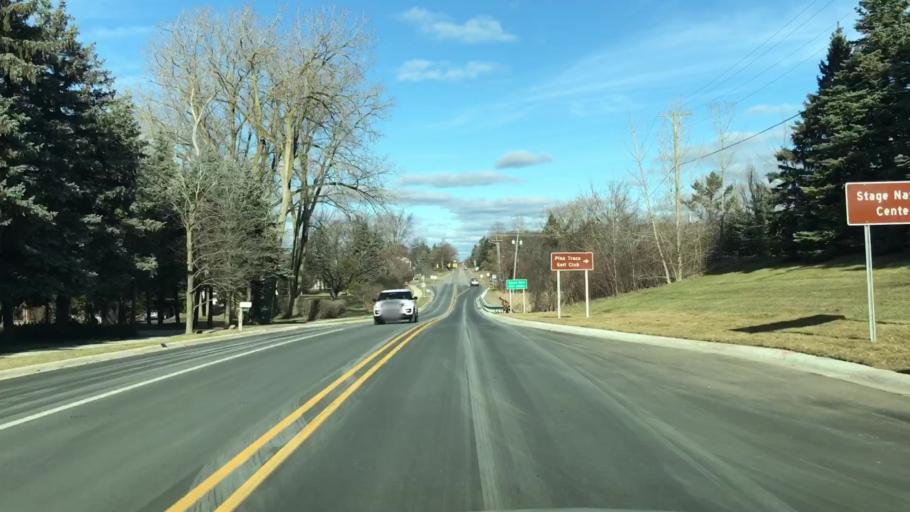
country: US
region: Michigan
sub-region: Oakland County
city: Bloomfield Hills
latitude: 42.6187
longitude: -83.2091
